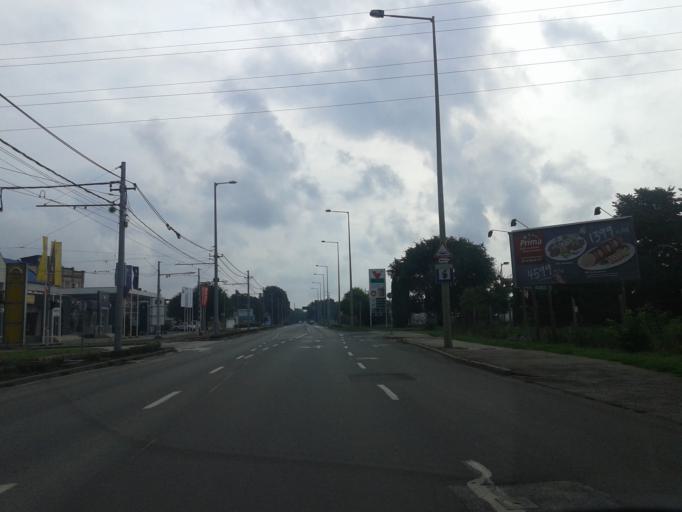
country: HU
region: Csongrad
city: Szeged
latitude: 46.2539
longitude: 20.1181
